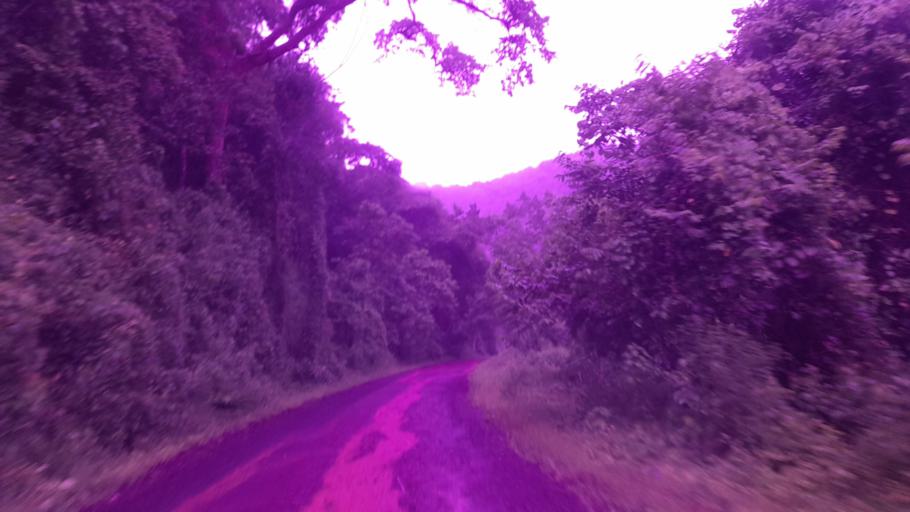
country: ET
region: Oromiya
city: Metu
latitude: 8.4798
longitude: 35.6474
